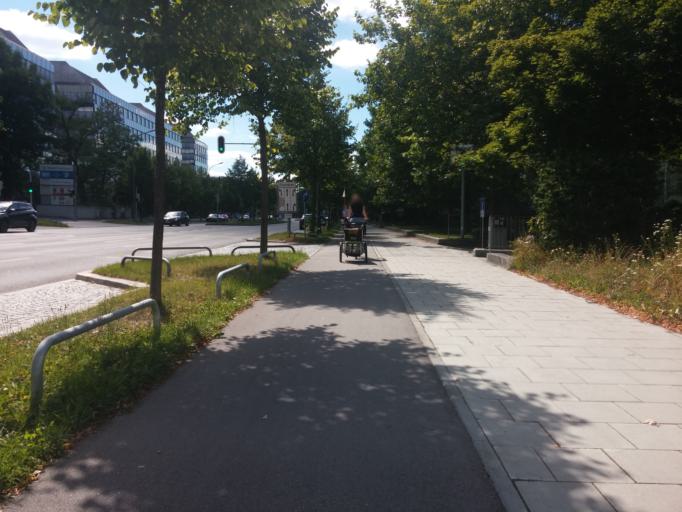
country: DE
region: Bavaria
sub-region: Upper Bavaria
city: Bogenhausen
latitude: 48.1490
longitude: 11.6197
